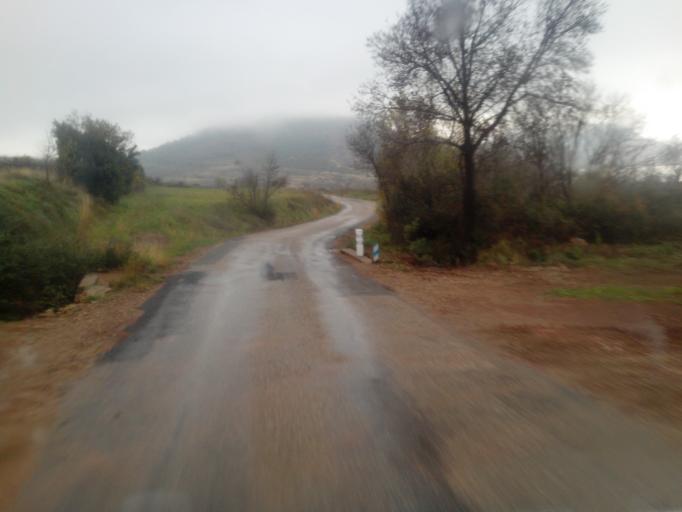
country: FR
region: Languedoc-Roussillon
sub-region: Departement de l'Herault
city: Lodeve
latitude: 43.6429
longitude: 3.3552
